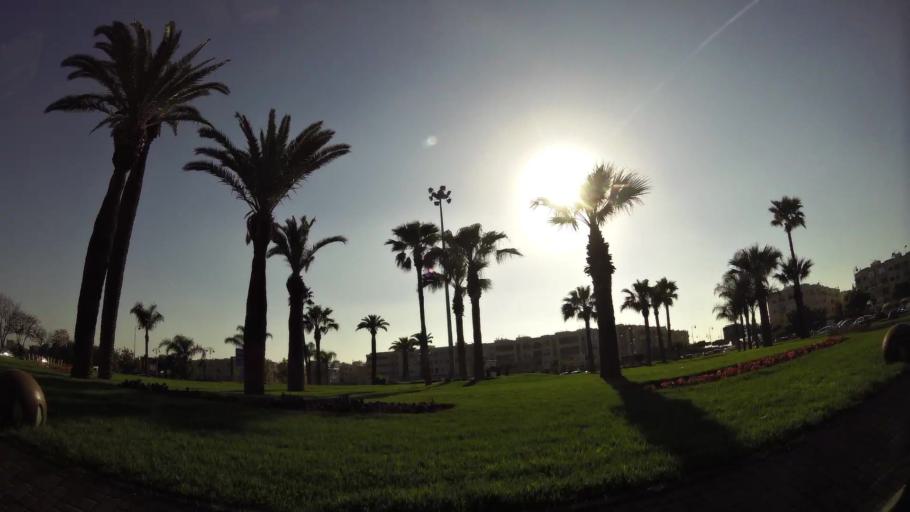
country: MA
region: Fes-Boulemane
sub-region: Fes
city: Fes
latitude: 34.0174
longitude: -5.0181
